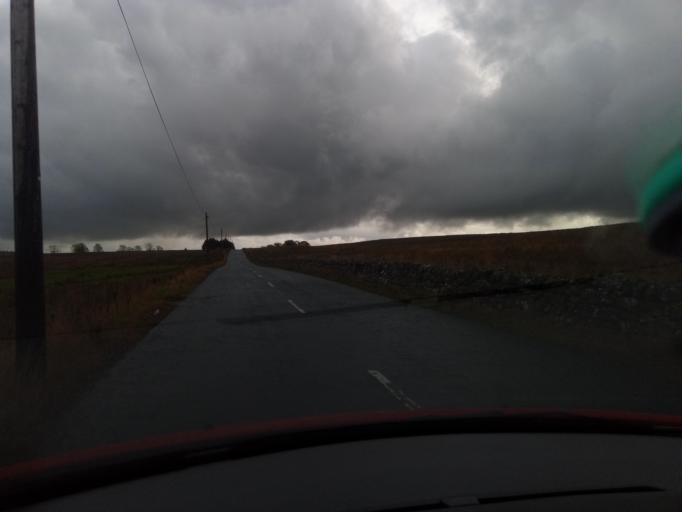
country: GB
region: England
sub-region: Northumberland
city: Birtley
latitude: 55.1302
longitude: -2.2429
